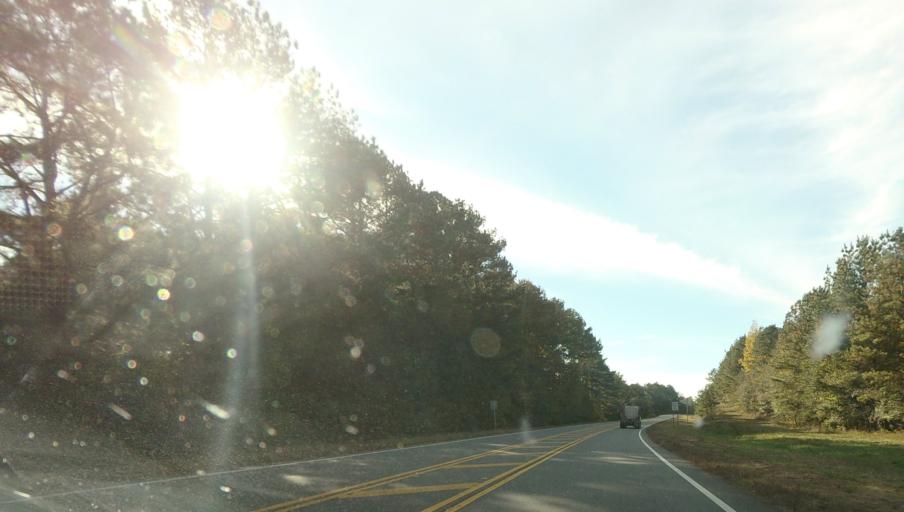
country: US
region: Georgia
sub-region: Talbot County
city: Talbotton
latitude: 32.6976
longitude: -84.4341
